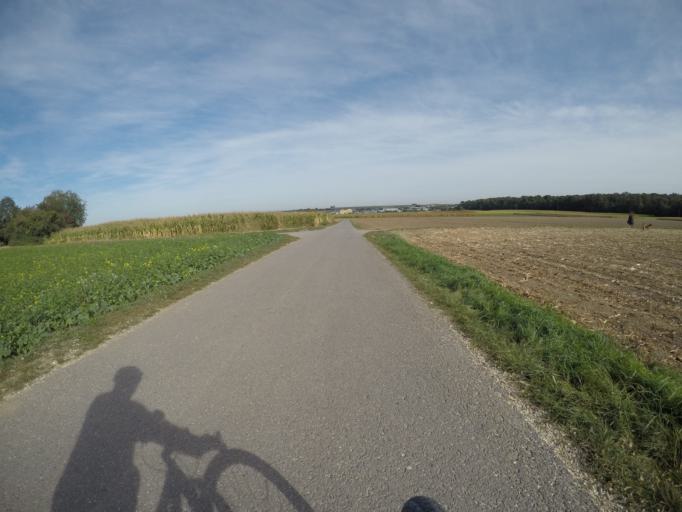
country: DE
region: Baden-Wuerttemberg
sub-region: Regierungsbezirk Stuttgart
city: Korntal
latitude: 48.8367
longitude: 9.1148
